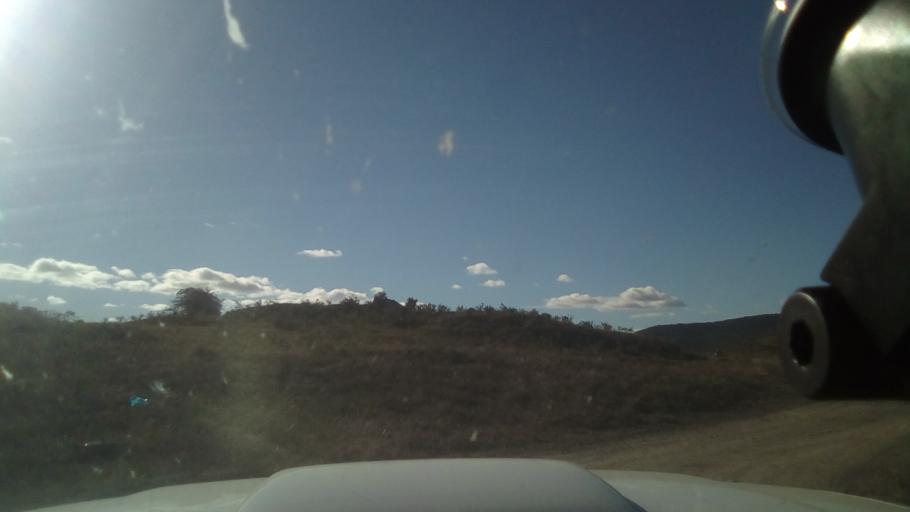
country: ZA
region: Eastern Cape
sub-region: Buffalo City Metropolitan Municipality
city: Bhisho
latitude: -32.7528
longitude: 27.3538
